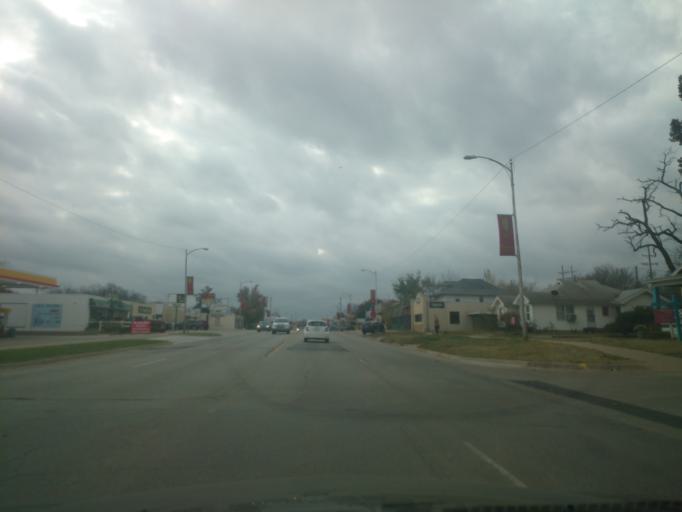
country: US
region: Oklahoma
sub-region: Payne County
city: Stillwater
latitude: 36.1222
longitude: -97.0588
